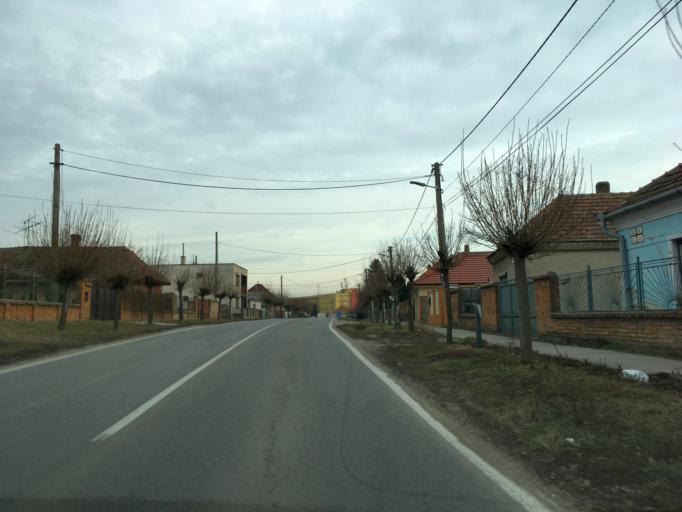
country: SK
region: Nitriansky
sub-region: Okres Nove Zamky
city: Nove Zamky
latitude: 47.9948
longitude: 18.2598
